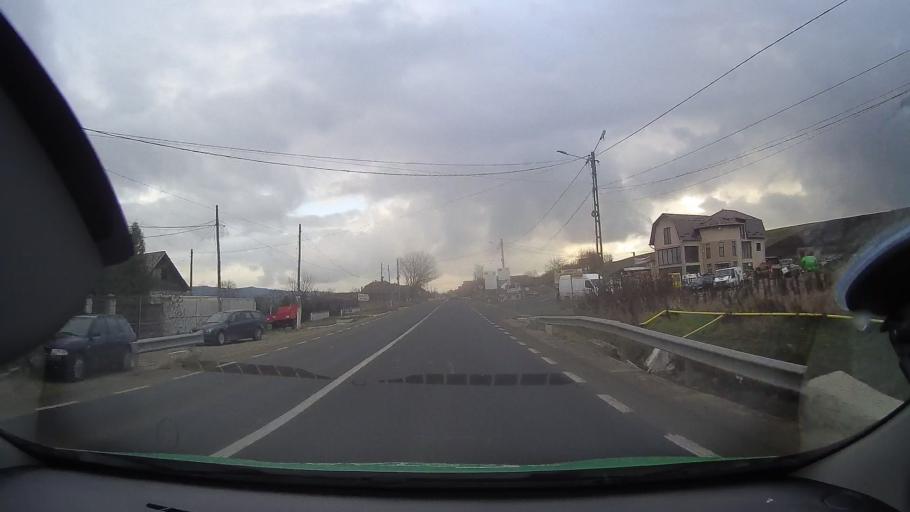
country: RO
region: Cluj
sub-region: Comuna Viisoara
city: Viisoara
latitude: 46.5158
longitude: 23.9156
